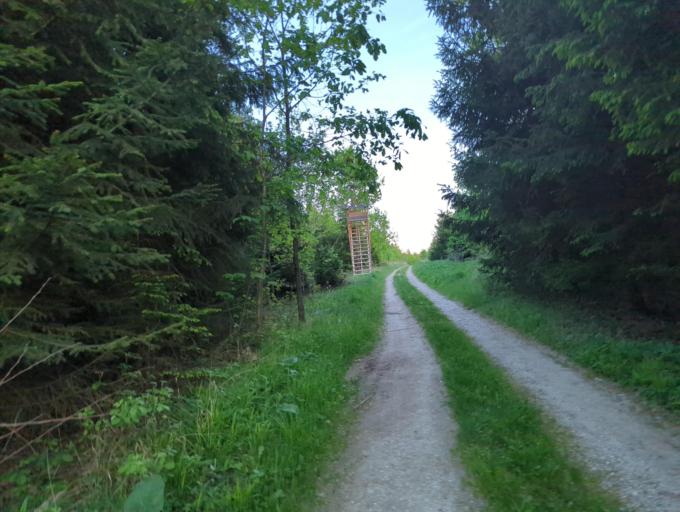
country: DE
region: Bavaria
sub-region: Upper Palatinate
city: Alteglofsheim
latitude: 48.9062
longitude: 12.1884
